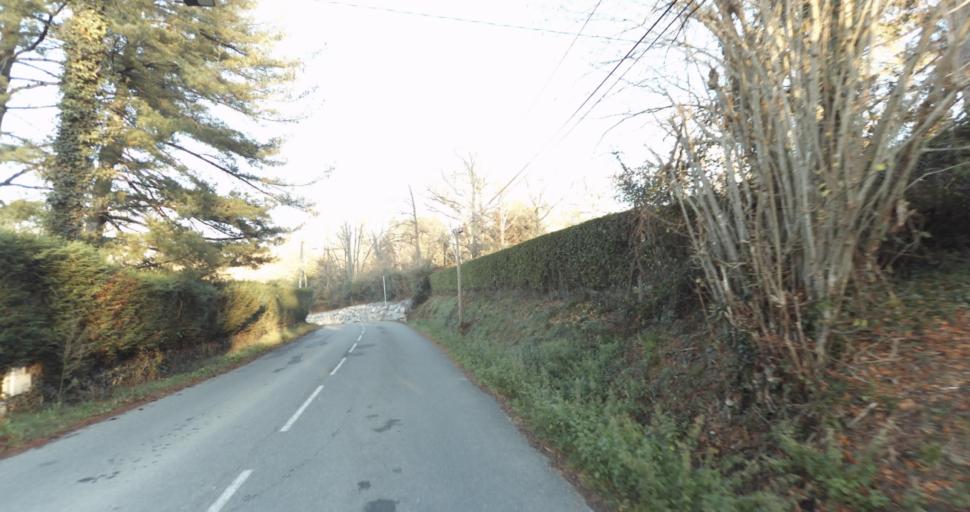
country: FR
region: Aquitaine
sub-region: Departement des Pyrenees-Atlantiques
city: Morlaas
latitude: 43.3296
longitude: -0.2702
